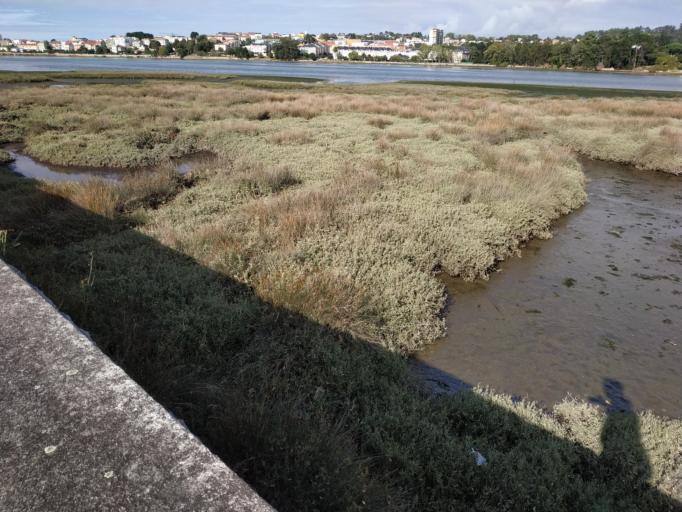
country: ES
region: Galicia
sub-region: Provincia da Coruna
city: Culleredo
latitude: 43.3224
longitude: -8.3743
